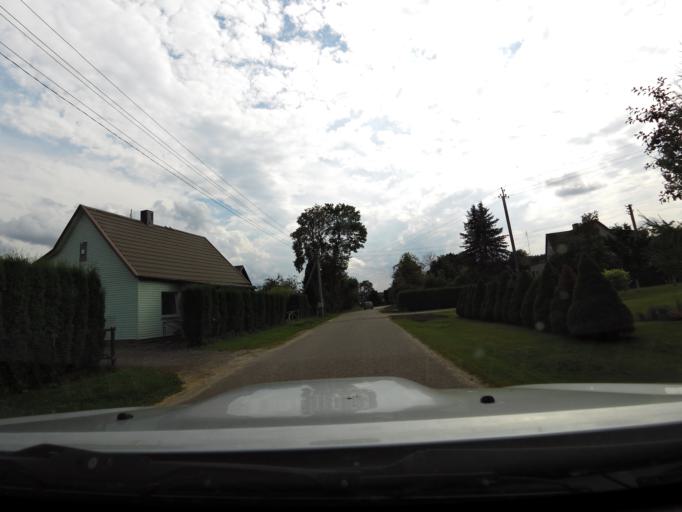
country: LT
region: Vilnius County
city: Elektrenai
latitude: 54.8384
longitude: 24.5748
